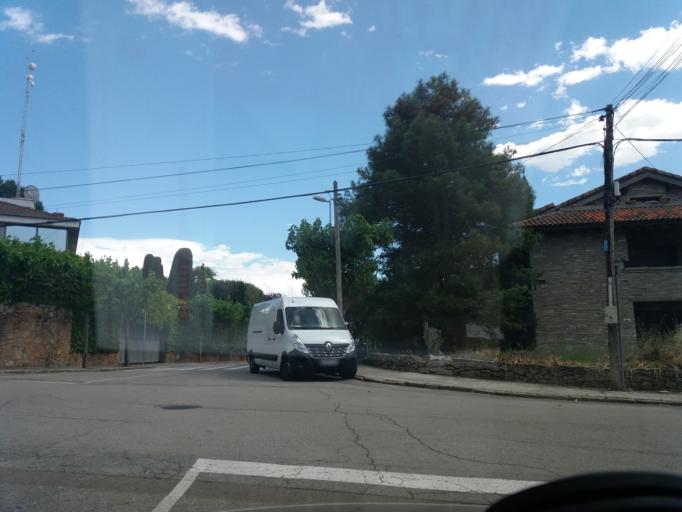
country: ES
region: Catalonia
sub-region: Provincia de Barcelona
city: Santpedor
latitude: 41.7566
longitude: 1.8389
